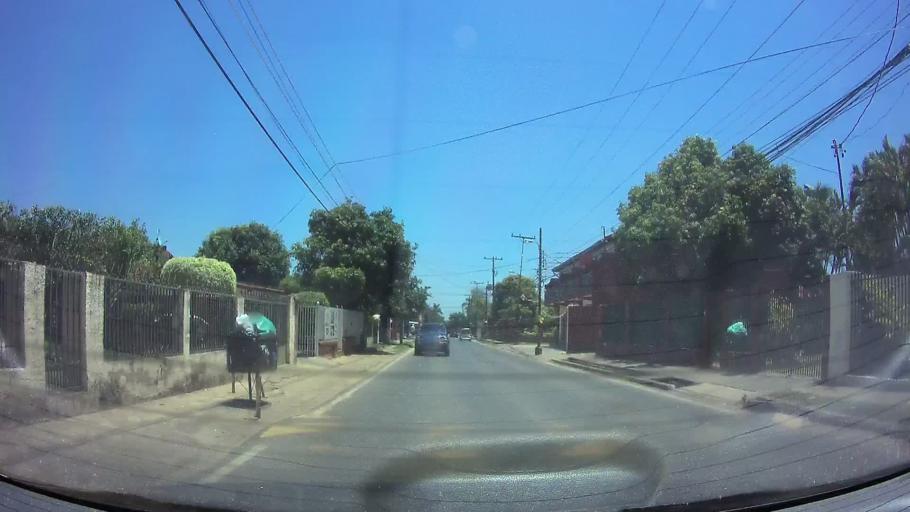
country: PY
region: Central
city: Fernando de la Mora
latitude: -25.2759
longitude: -57.5190
